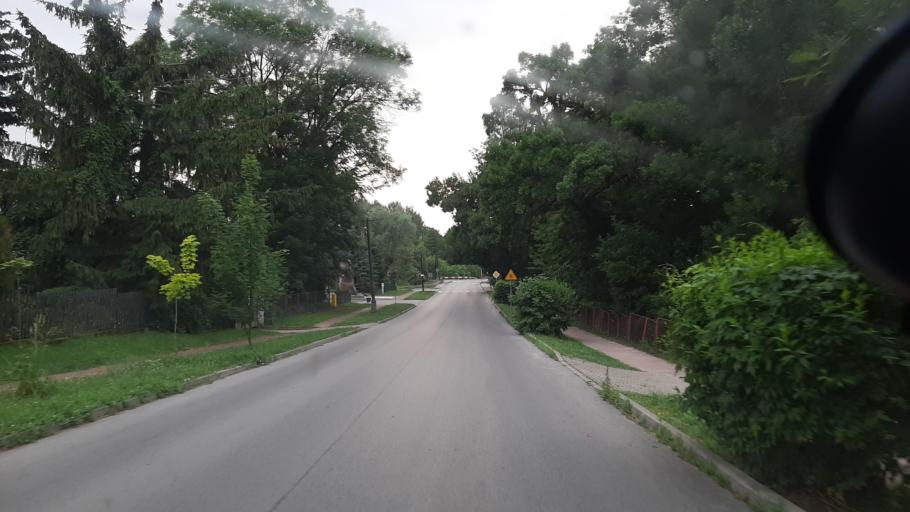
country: PL
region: Lublin Voivodeship
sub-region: Powiat lubelski
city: Garbow
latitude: 51.3515
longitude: 22.3377
